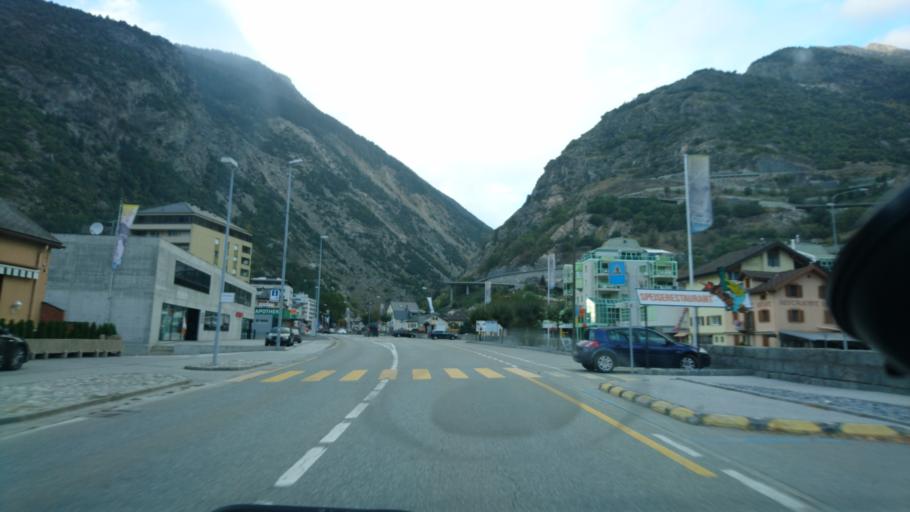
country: CH
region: Valais
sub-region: Leuk District
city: Gampel
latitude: 46.3141
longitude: 7.7448
